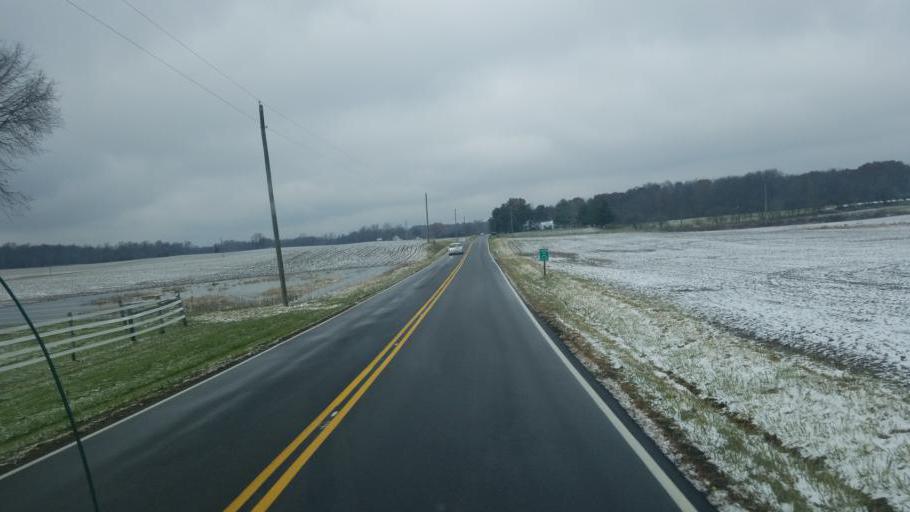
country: US
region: Ohio
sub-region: Richland County
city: Ontario
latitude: 40.8133
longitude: -82.6287
